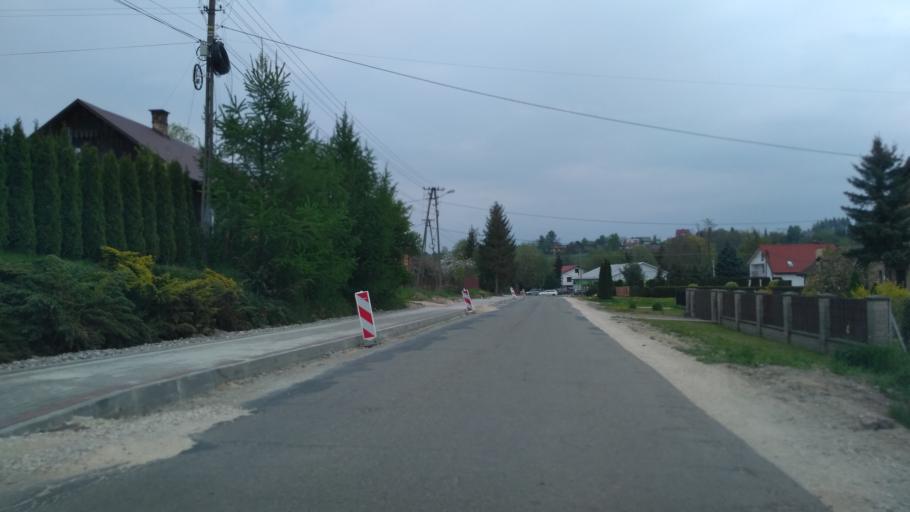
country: PL
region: Lesser Poland Voivodeship
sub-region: Powiat tarnowski
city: Skrzyszow
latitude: 49.9763
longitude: 21.0633
